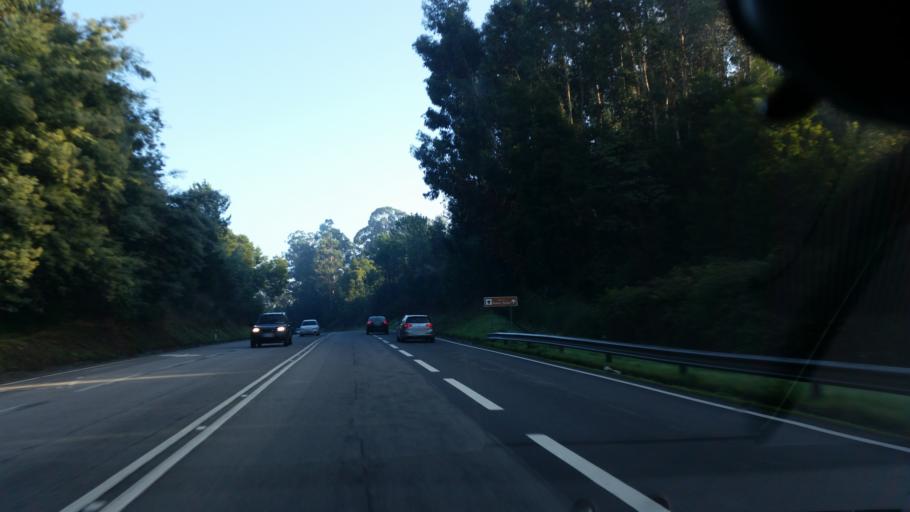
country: PT
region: Porto
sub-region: Santo Tirso
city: Sao Miguel do Couto
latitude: 41.3336
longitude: -8.4685
